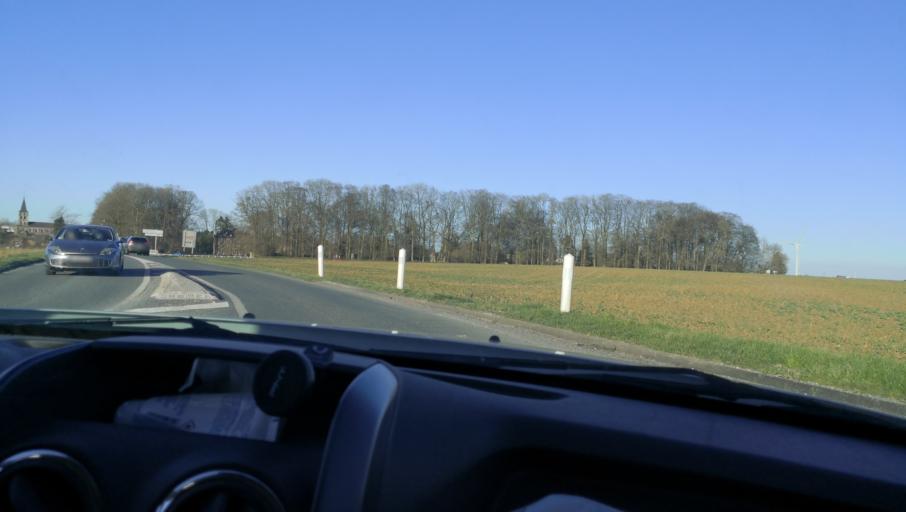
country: FR
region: Haute-Normandie
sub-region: Departement de la Seine-Maritime
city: Totes
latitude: 49.6729
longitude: 1.0445
